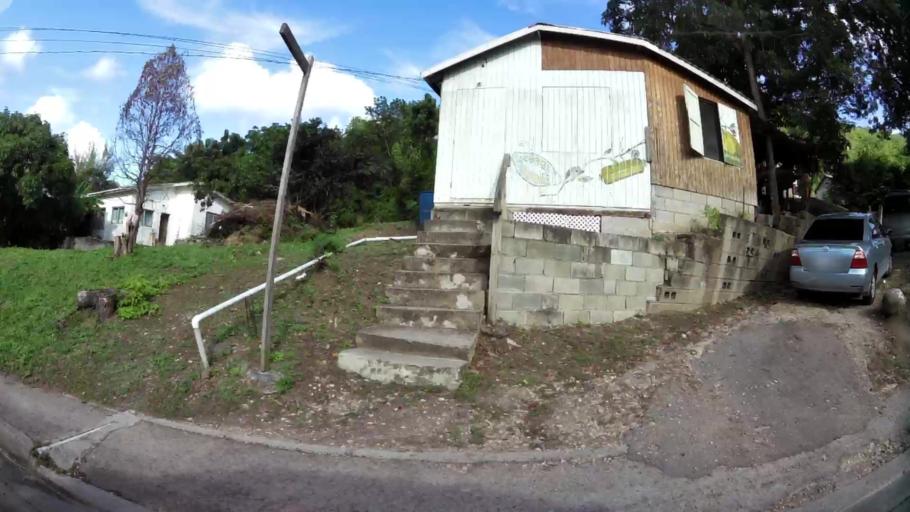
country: AG
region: Saint Paul
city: Liberta
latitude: 17.0327
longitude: -61.7884
